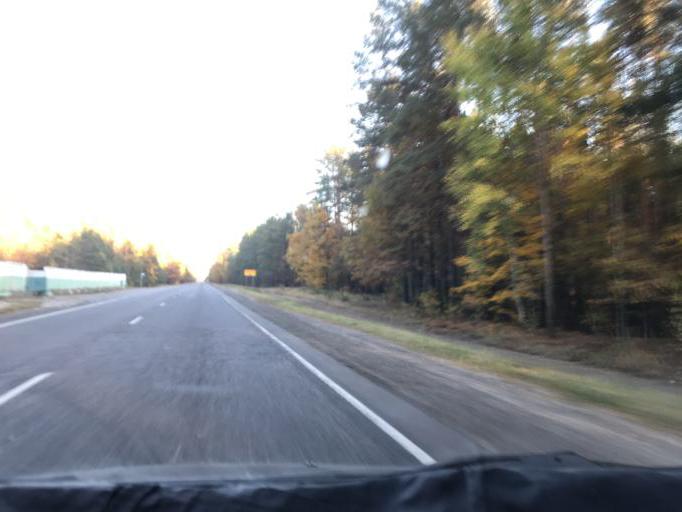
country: BY
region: Gomel
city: Zhytkavichy
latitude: 52.2748
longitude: 28.1822
